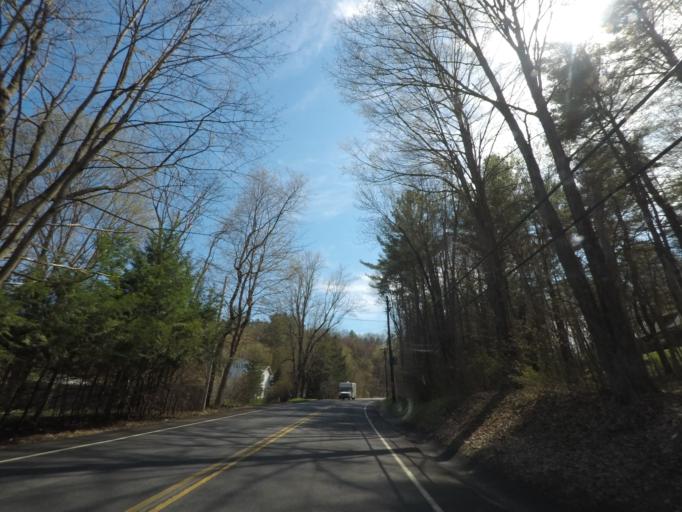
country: US
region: New York
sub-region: Columbia County
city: Chatham
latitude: 42.4038
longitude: -73.5256
